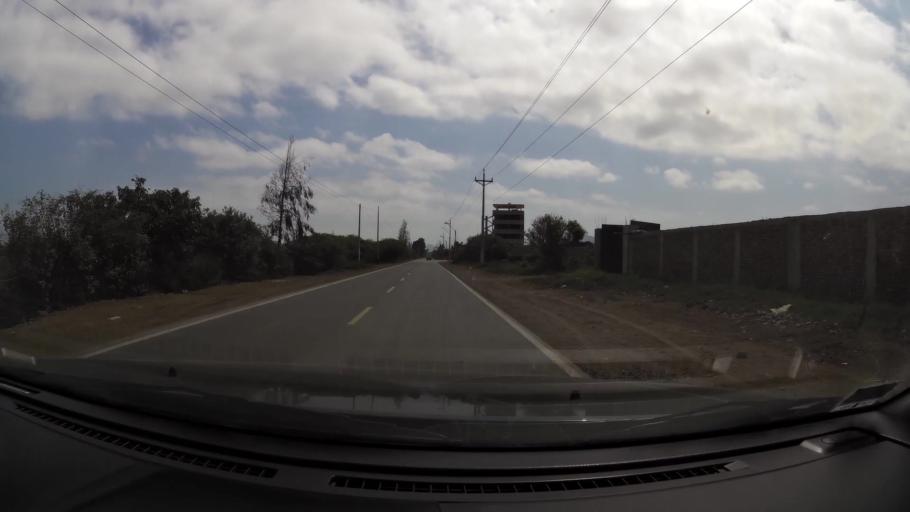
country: PE
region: Lima
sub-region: Provincia de Canete
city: Mala
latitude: -12.6993
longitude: -76.6233
